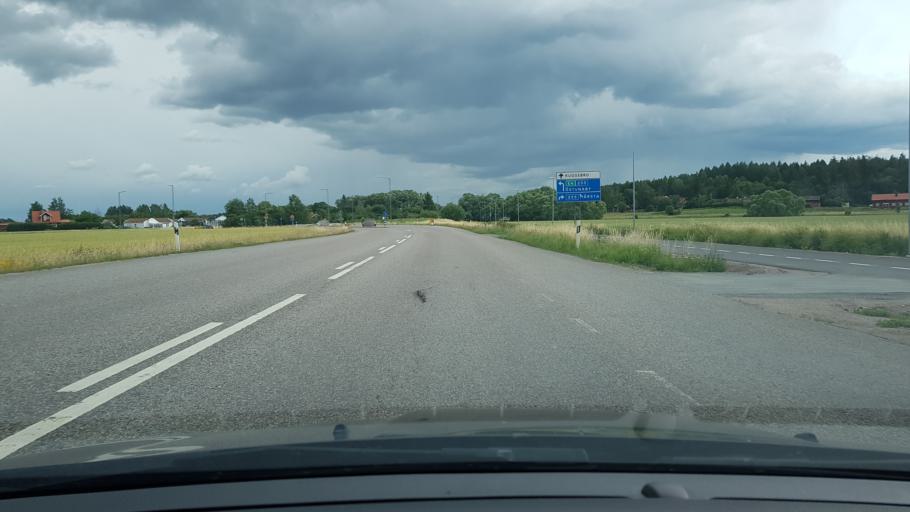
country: SE
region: Uppsala
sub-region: Uppsala Kommun
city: Saevja
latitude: 59.8349
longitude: 17.6881
